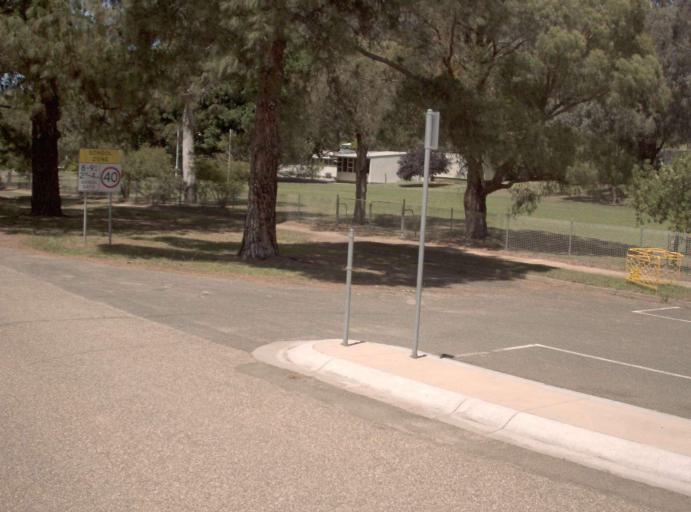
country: AU
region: Victoria
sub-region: East Gippsland
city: Bairnsdale
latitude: -37.2645
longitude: 147.7224
